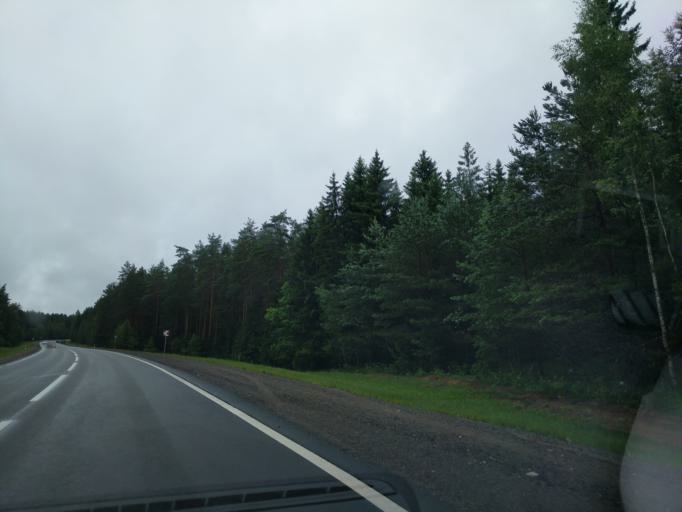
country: BY
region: Minsk
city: Syomkava
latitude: 54.1955
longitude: 27.4992
